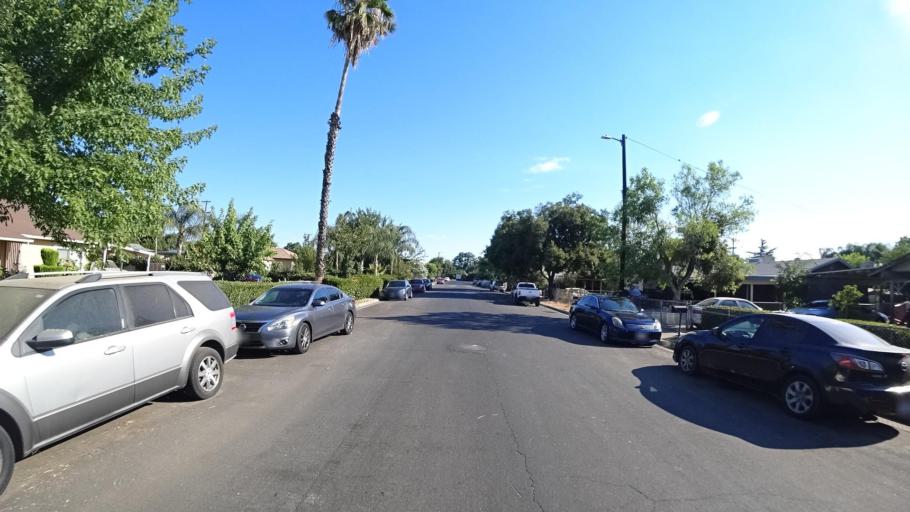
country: US
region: California
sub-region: Fresno County
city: Fresno
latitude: 36.7119
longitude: -119.7426
